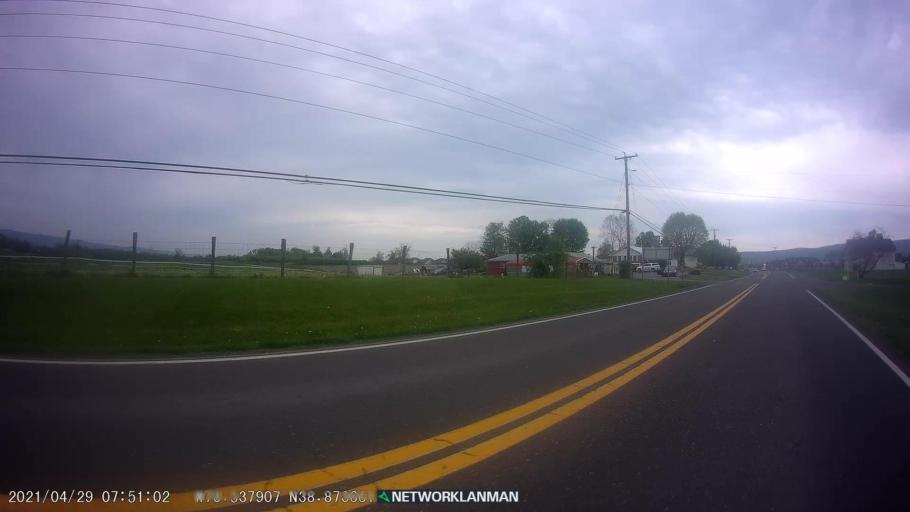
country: US
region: Virginia
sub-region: Shenandoah County
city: Woodstock
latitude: 38.8736
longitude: -78.5376
